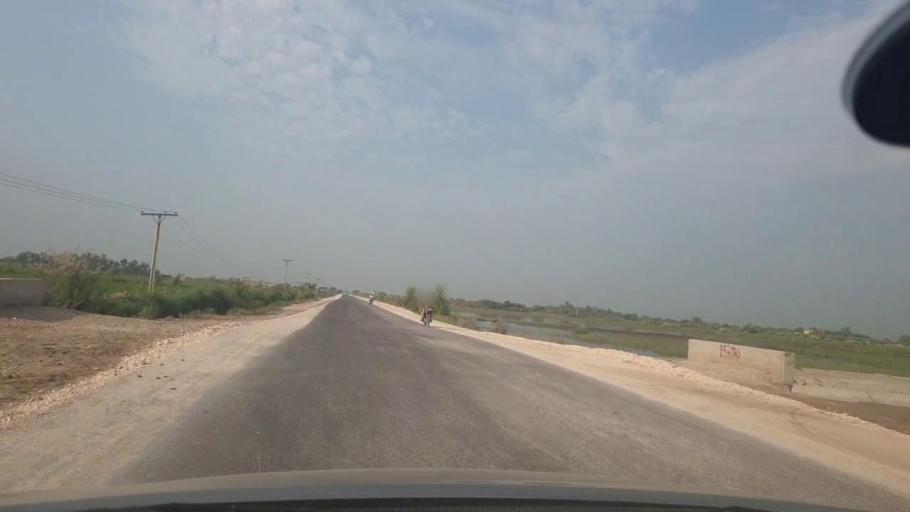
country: PK
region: Sindh
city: Jacobabad
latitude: 28.1432
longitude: 68.3441
